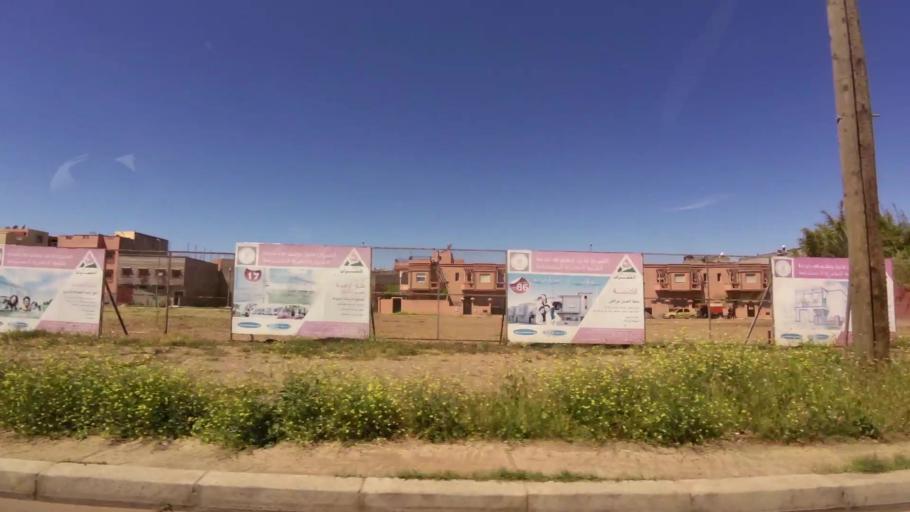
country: MA
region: Marrakech-Tensift-Al Haouz
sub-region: Marrakech
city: Marrakesh
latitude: 31.5726
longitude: -7.9809
